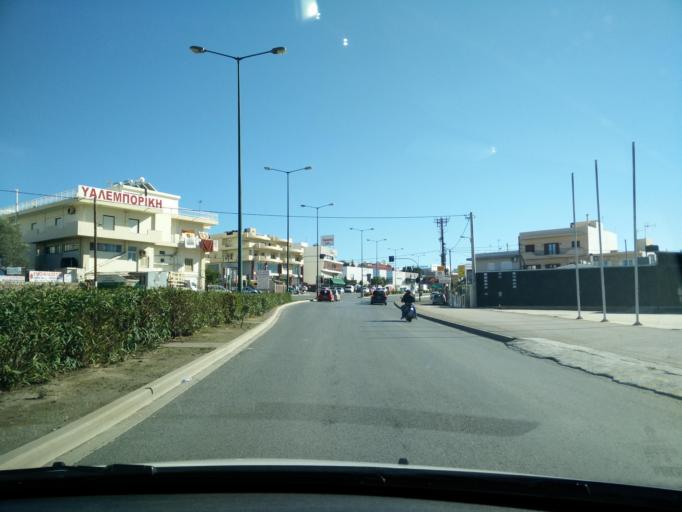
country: GR
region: Crete
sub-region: Nomos Irakleiou
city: Nea Alikarnassos
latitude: 35.3360
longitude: 25.1563
